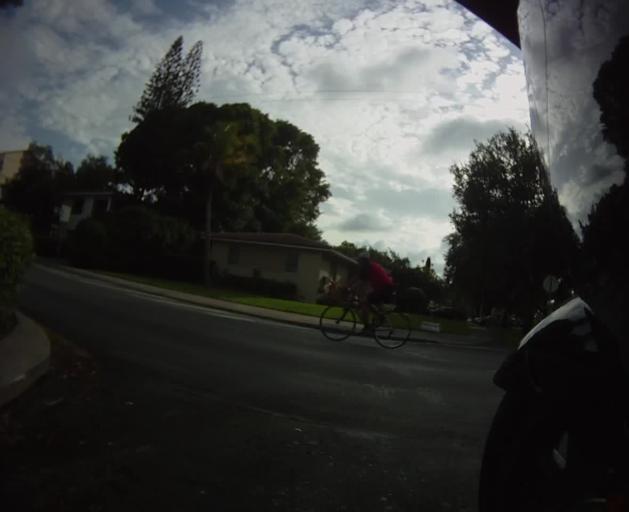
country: US
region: Florida
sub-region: Miami-Dade County
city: Coral Gables
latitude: 25.7357
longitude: -80.2587
